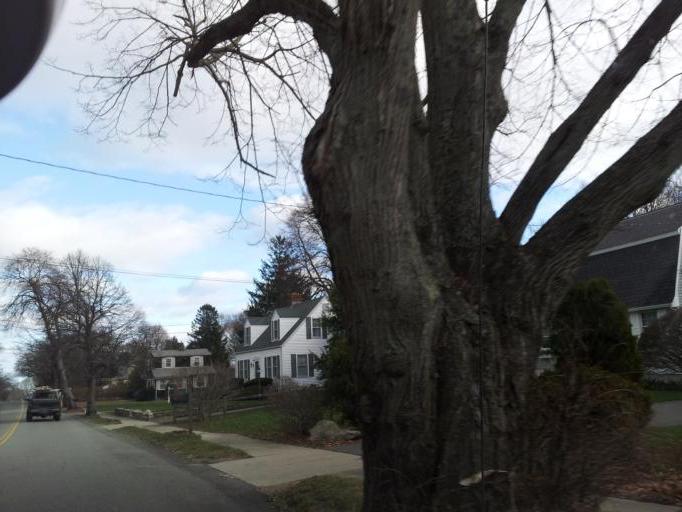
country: US
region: Massachusetts
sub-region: Plymouth County
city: Plymouth
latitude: 41.9435
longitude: -70.6491
